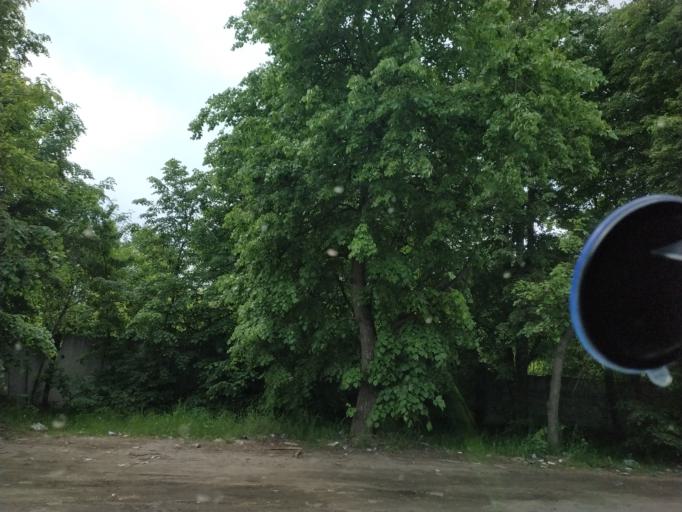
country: RU
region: Moskovskaya
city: Zhukovskiy
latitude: 55.5577
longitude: 38.1134
